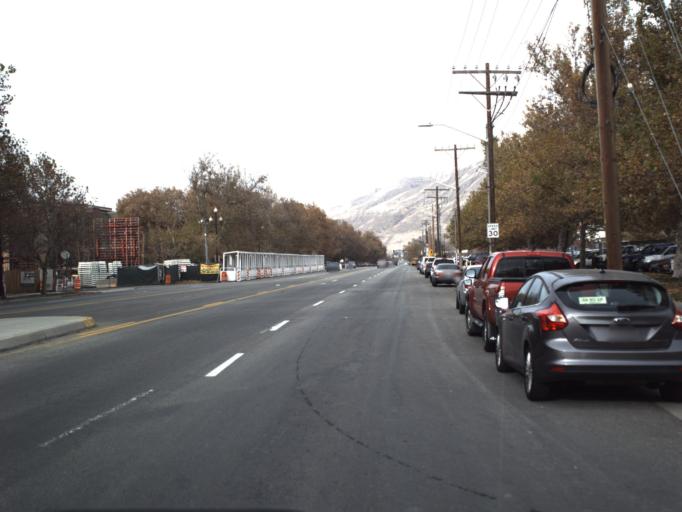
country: US
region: Utah
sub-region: Salt Lake County
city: Salt Lake City
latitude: 40.7720
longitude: -111.9024
